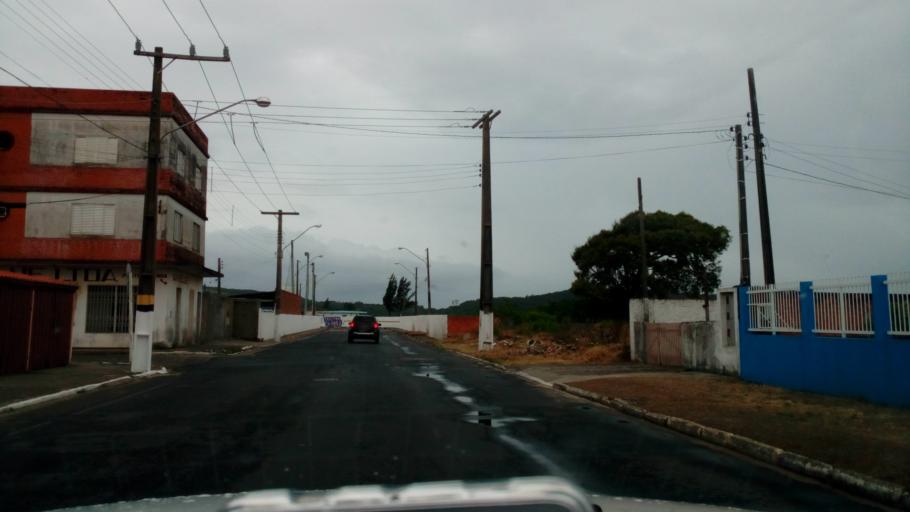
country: BR
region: Santa Catarina
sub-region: Laguna
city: Laguna
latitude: -28.4956
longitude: -48.7754
